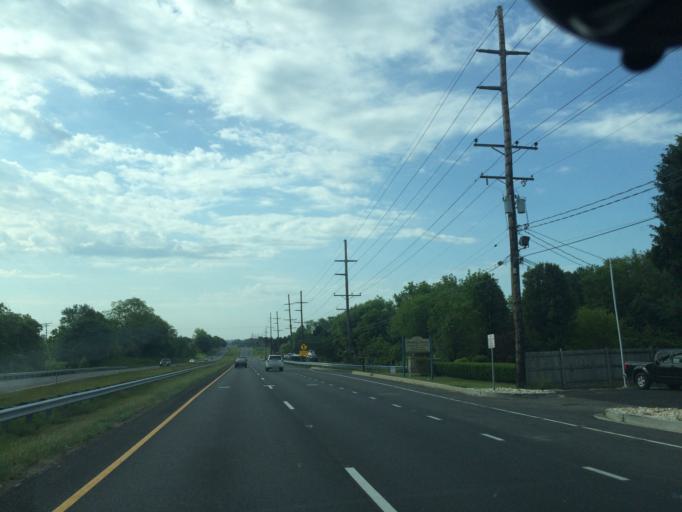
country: US
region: Maryland
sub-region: Baltimore County
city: Reisterstown
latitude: 39.5134
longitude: -76.9093
